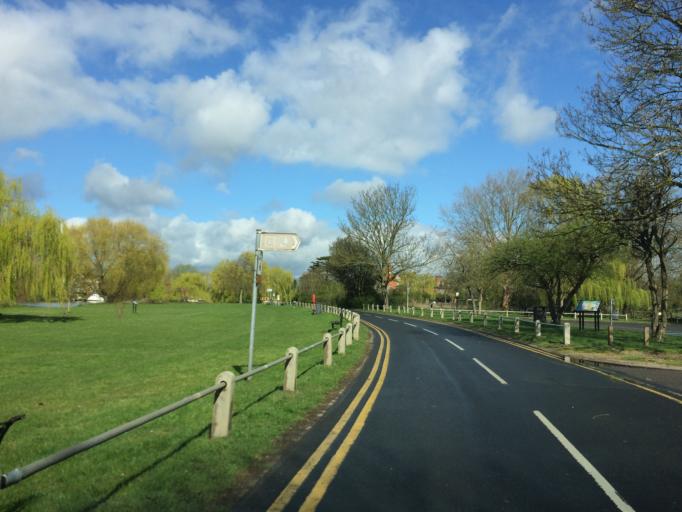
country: GB
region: England
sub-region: Surrey
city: Chertsey
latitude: 51.4047
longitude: -0.4910
